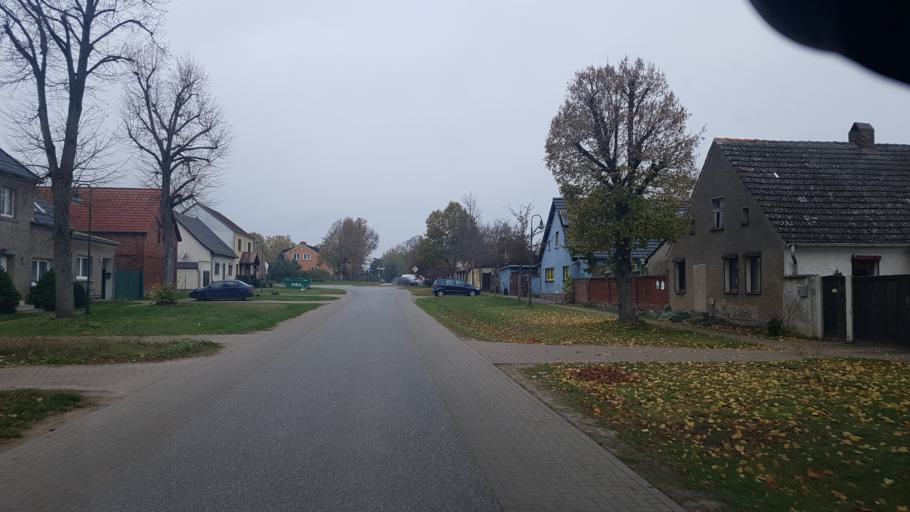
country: DE
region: Brandenburg
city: Schonermark
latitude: 52.9334
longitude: 13.1026
